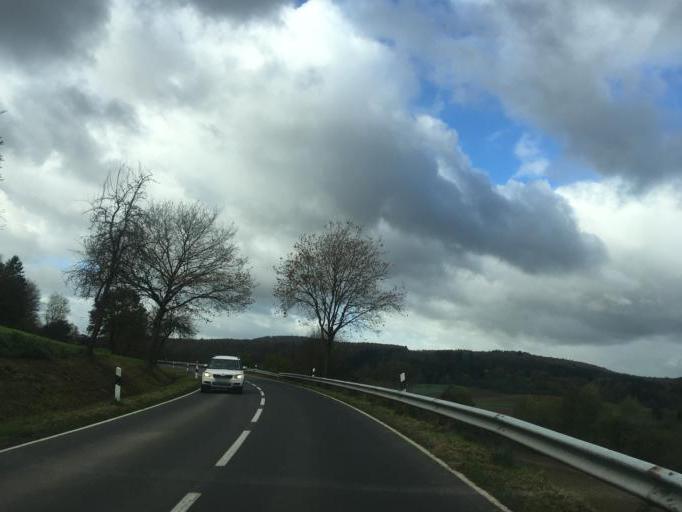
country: DE
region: Lower Saxony
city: Bodenfelde
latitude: 51.6492
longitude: 9.5452
